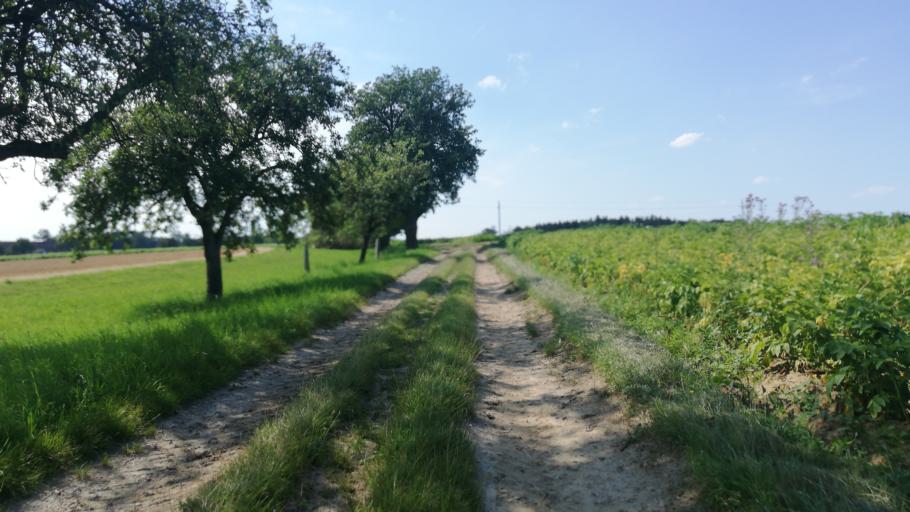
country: AT
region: Upper Austria
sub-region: Wels-Land
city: Gunskirchen
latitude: 48.1626
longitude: 13.9284
